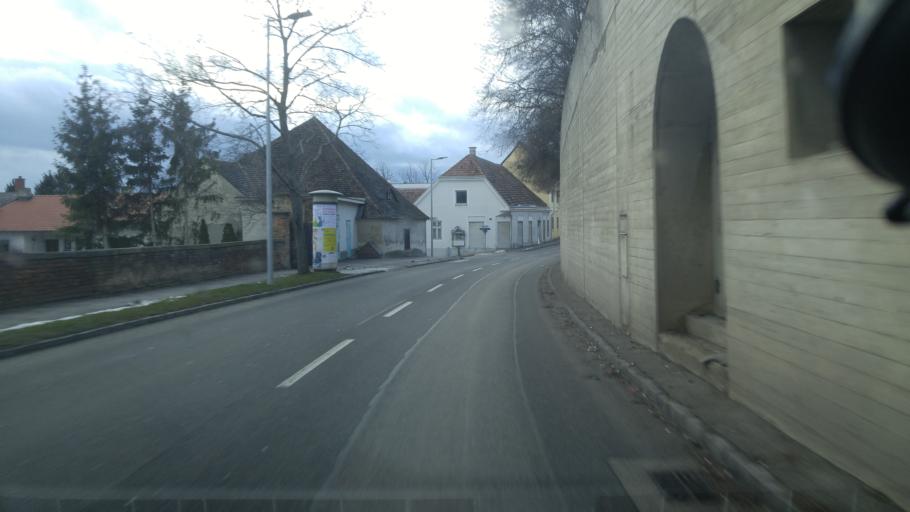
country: AT
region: Lower Austria
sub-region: Politischer Bezirk Baden
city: Bad Voslau
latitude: 47.9634
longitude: 16.2032
